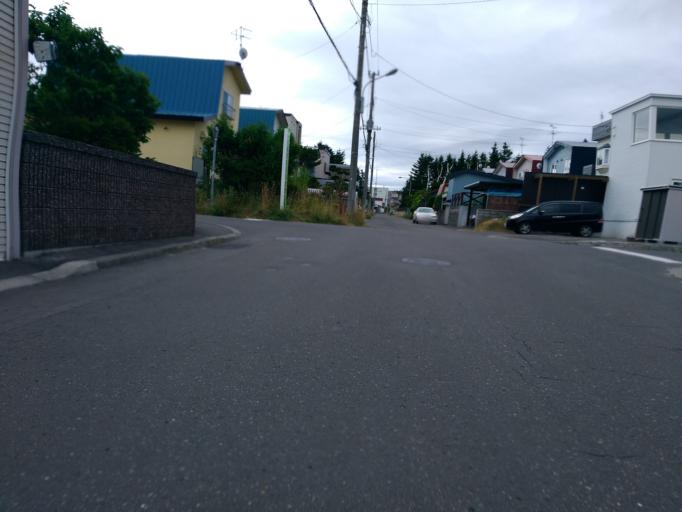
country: JP
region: Hokkaido
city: Ebetsu
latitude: 43.0831
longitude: 141.5258
